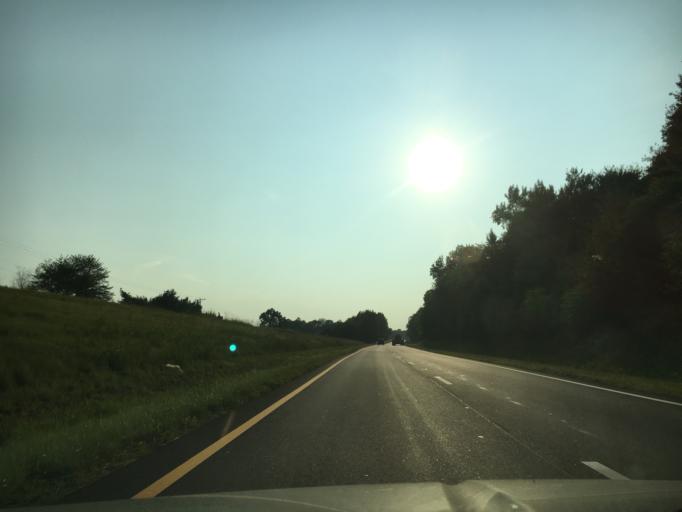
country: US
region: Virginia
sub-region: Prince Edward County
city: Hampden Sydney
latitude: 37.3036
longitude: -78.5404
